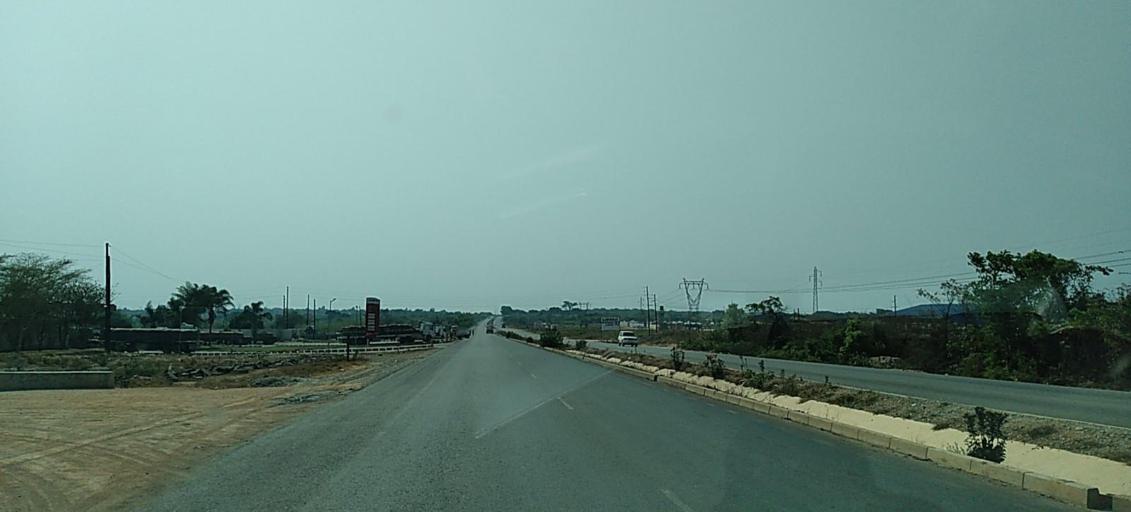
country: ZM
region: Copperbelt
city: Chingola
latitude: -12.5735
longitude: 27.9142
